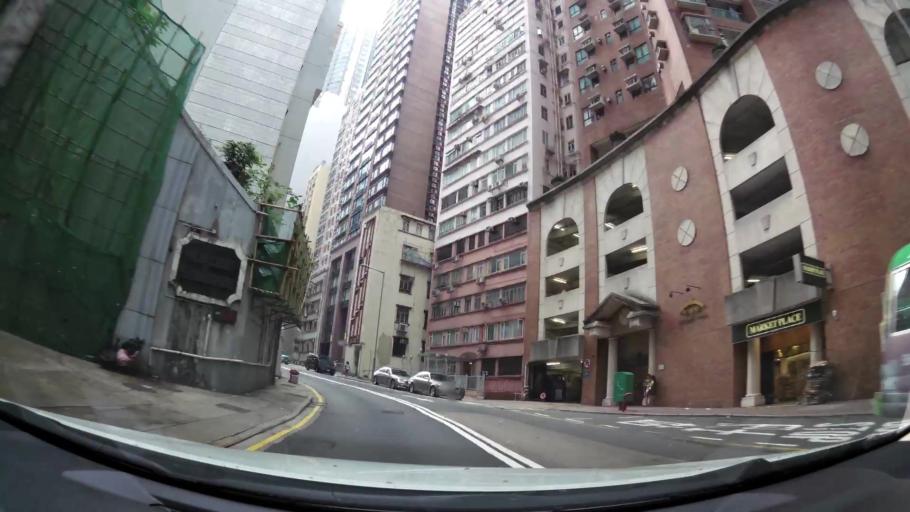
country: HK
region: Central and Western
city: Central
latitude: 22.2804
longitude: 114.1512
